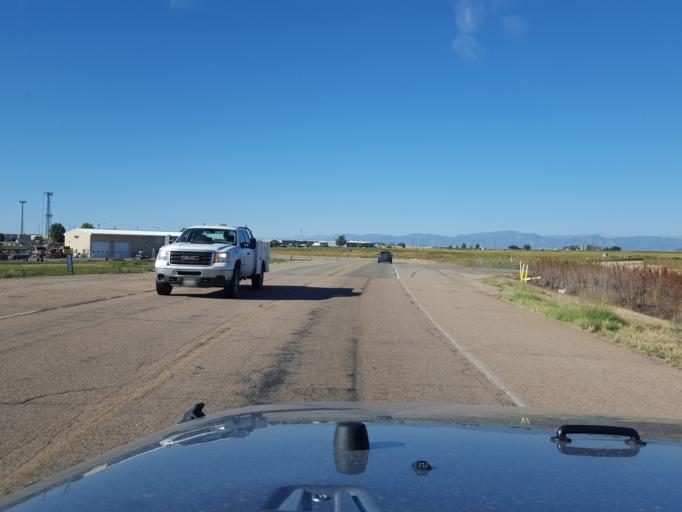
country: US
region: Colorado
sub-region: Weld County
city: Dacono
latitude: 40.0909
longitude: -104.9822
